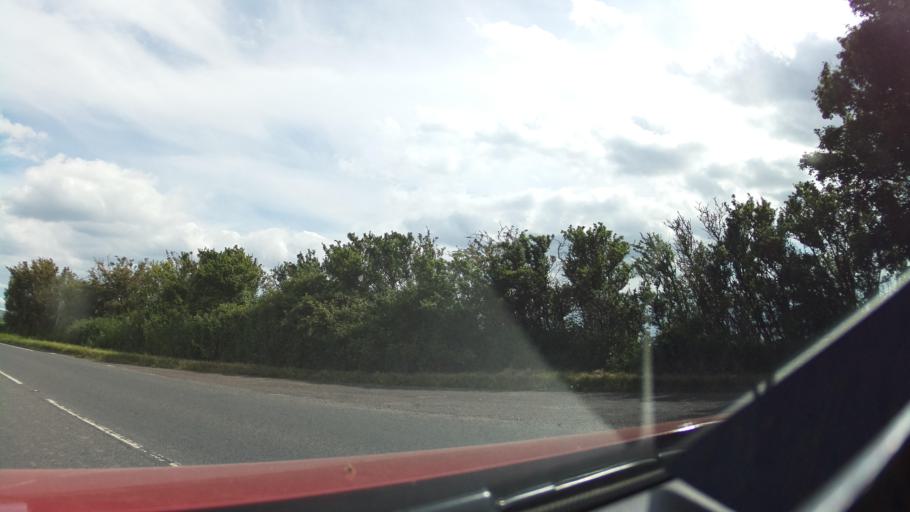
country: GB
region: England
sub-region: Worcestershire
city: Pershore
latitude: 52.1218
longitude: -2.1029
